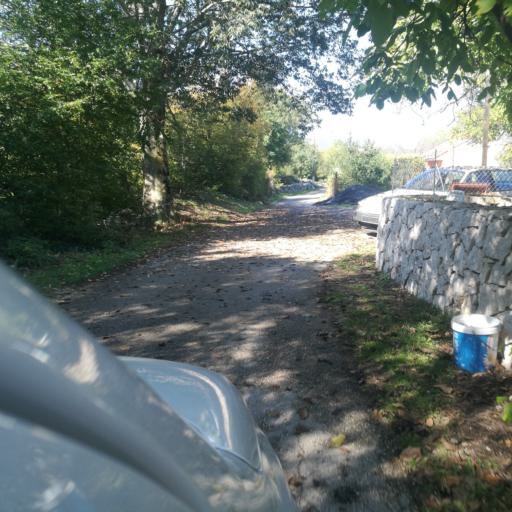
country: HR
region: Splitsko-Dalmatinska
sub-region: Grad Omis
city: Omis
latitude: 43.5164
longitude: 16.7531
